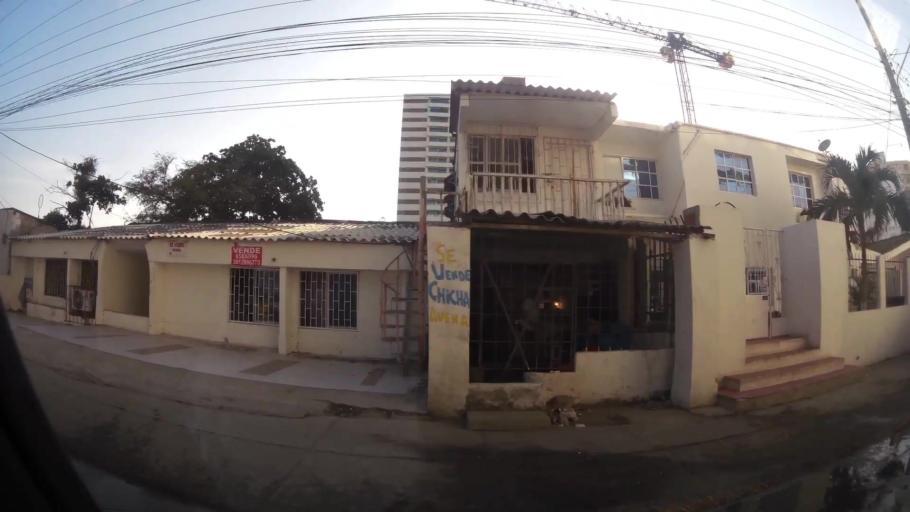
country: CO
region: Bolivar
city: Cartagena
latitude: 10.4348
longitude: -75.5352
